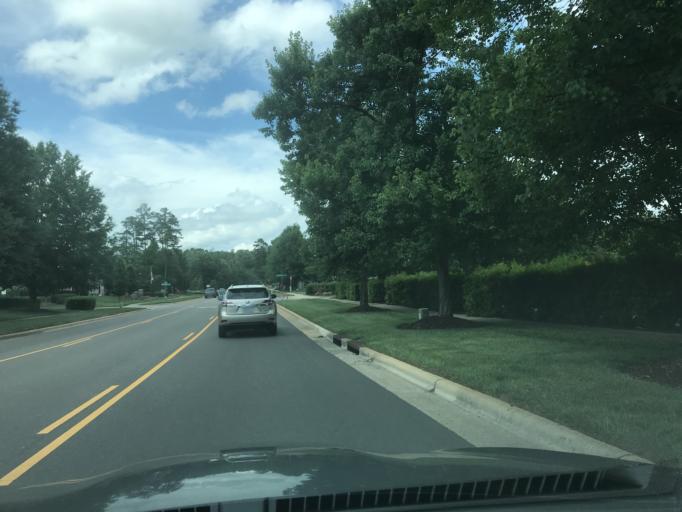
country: US
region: North Carolina
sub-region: Wake County
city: Wake Forest
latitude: 35.9077
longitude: -78.5909
